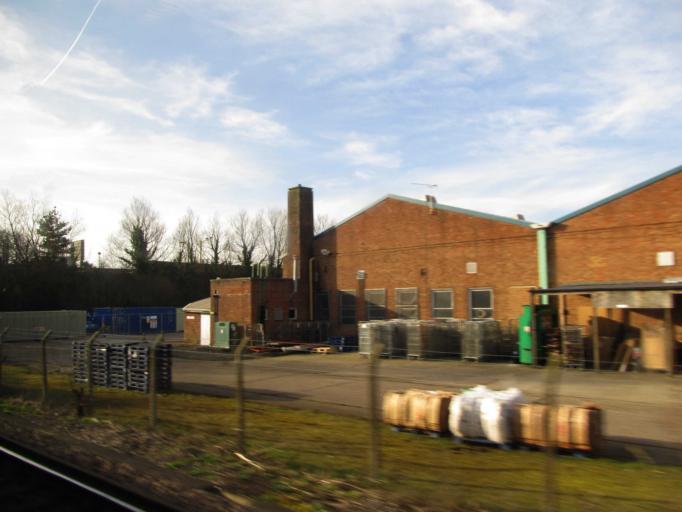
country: GB
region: England
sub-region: Surrey
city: Frimley
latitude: 51.3162
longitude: -0.7616
